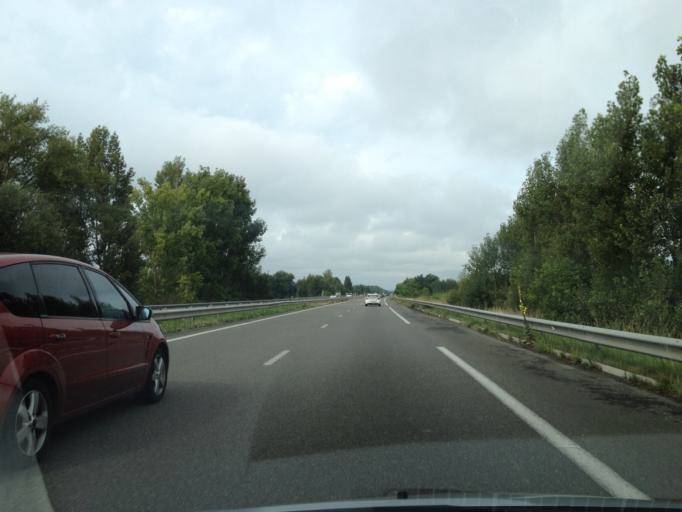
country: FR
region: Midi-Pyrenees
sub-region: Departement du Tarn-et-Garonne
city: Castelsarrasin
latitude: 44.0473
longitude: 1.0796
